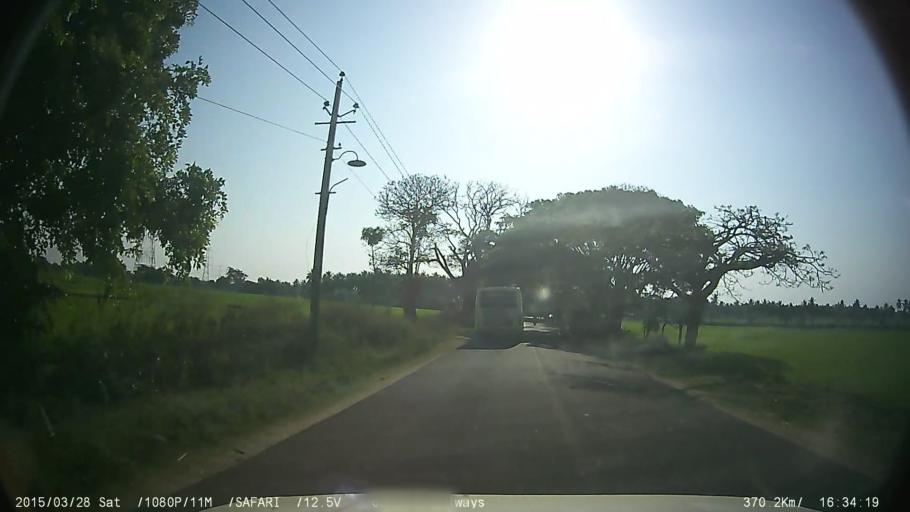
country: IN
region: Karnataka
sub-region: Mandya
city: Shrirangapattana
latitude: 12.3918
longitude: 76.6193
